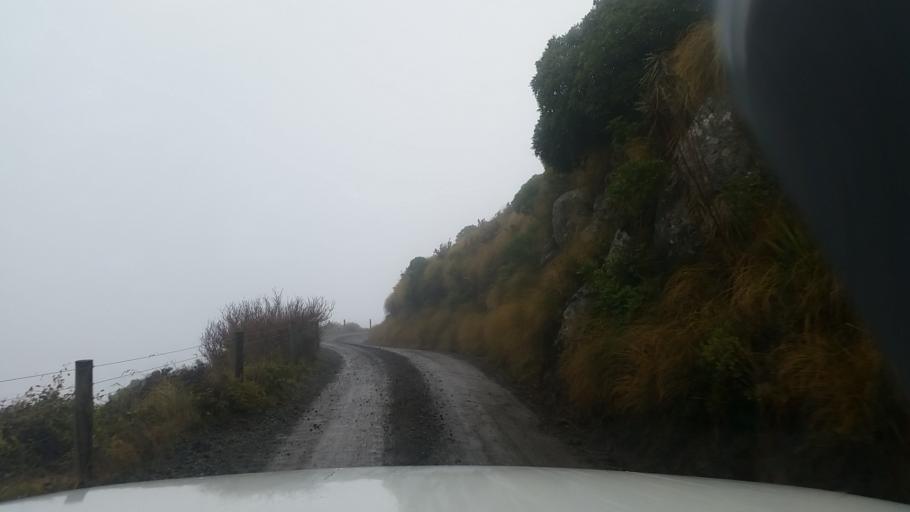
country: NZ
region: Canterbury
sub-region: Christchurch City
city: Christchurch
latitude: -43.8118
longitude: 172.8187
